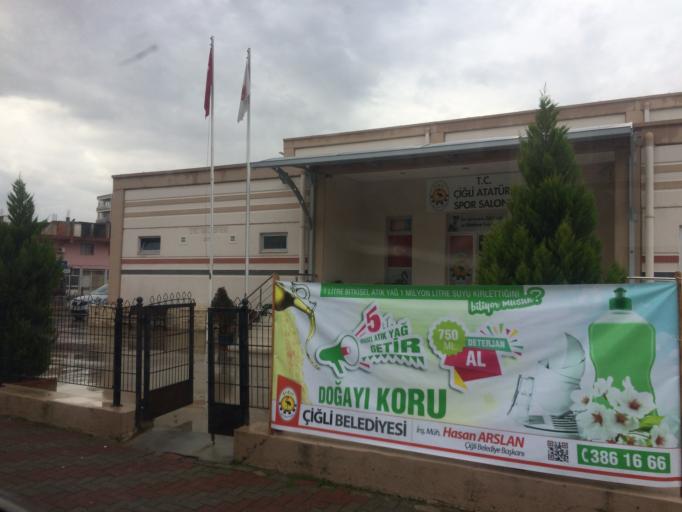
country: TR
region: Izmir
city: Karsiyaka
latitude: 38.4918
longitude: 27.0570
